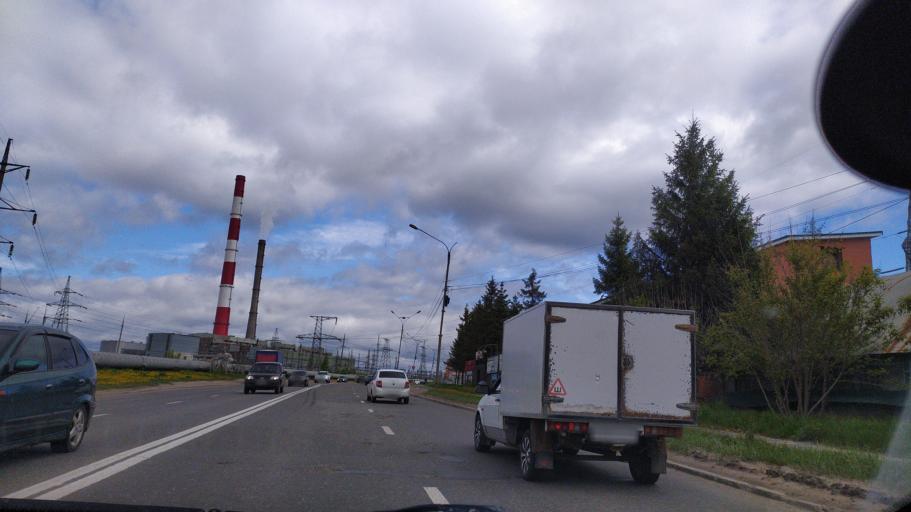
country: RU
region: Chuvashia
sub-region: Cheboksarskiy Rayon
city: Cheboksary
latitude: 56.1181
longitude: 47.3019
